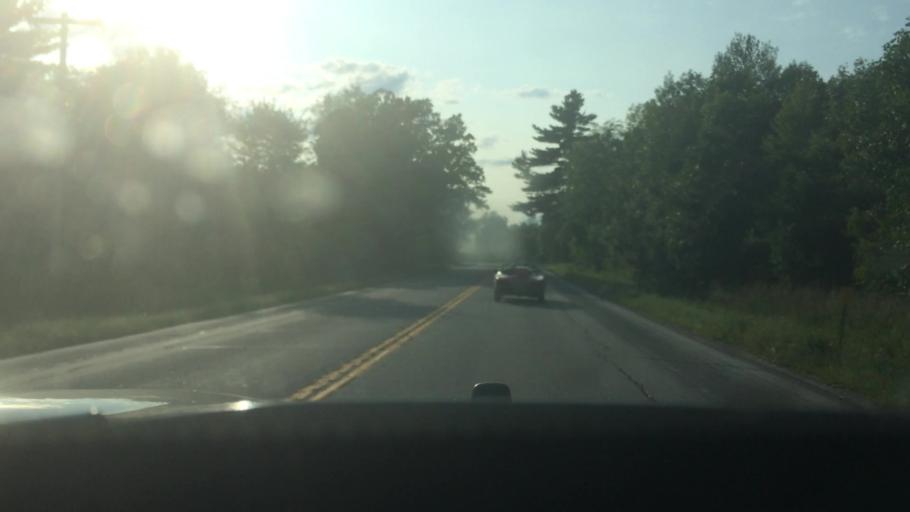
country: US
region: New York
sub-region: St. Lawrence County
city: Canton
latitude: 44.6490
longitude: -75.2920
